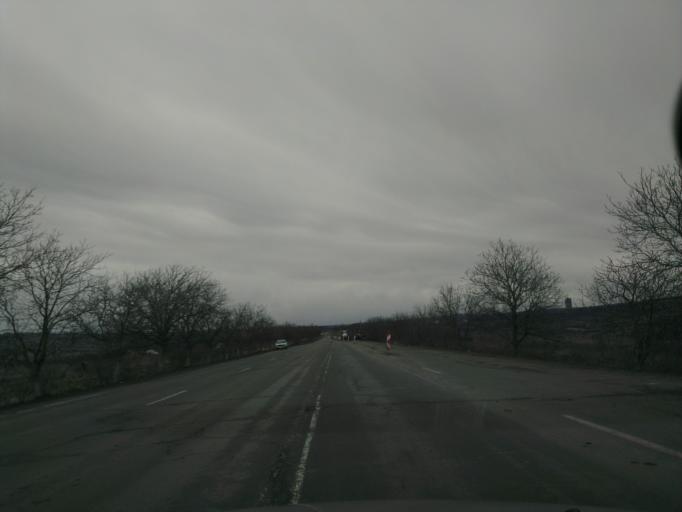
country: MD
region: Laloveni
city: Ialoveni
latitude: 46.9939
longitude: 28.7377
